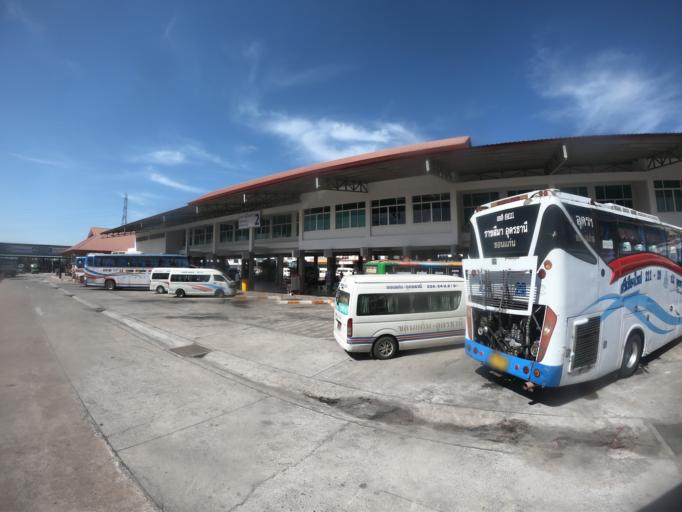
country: TH
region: Khon Kaen
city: Khon Kaen
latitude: 16.3902
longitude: 102.8043
